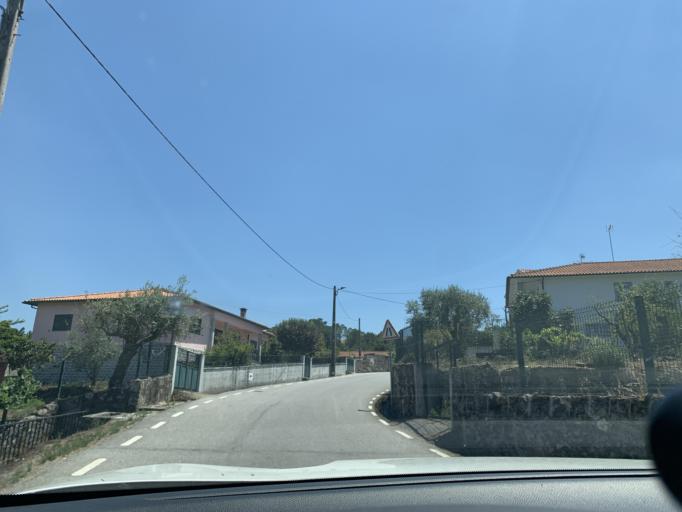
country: PT
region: Viseu
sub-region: Mangualde
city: Mangualde
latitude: 40.5587
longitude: -7.7232
